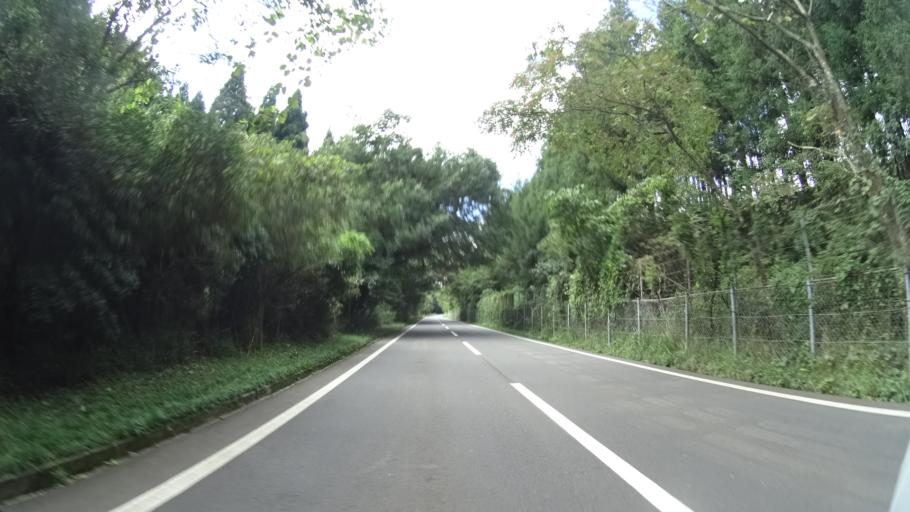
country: JP
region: Oita
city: Beppu
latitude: 33.3357
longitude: 131.4255
